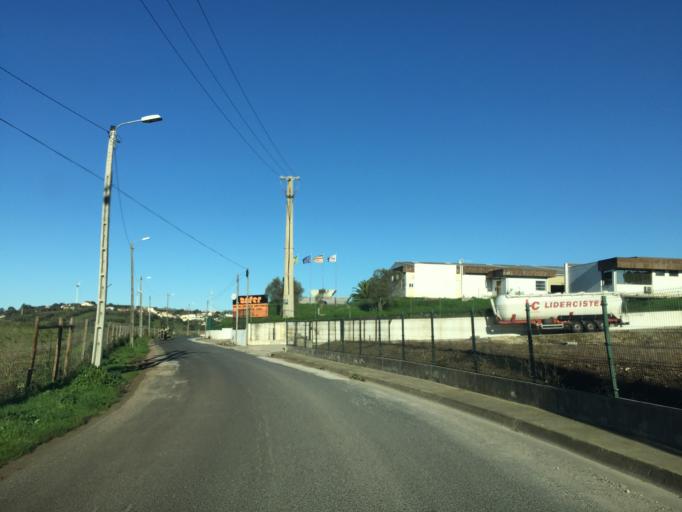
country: PT
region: Lisbon
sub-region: Odivelas
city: Canecas
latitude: 38.8280
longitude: -9.2474
